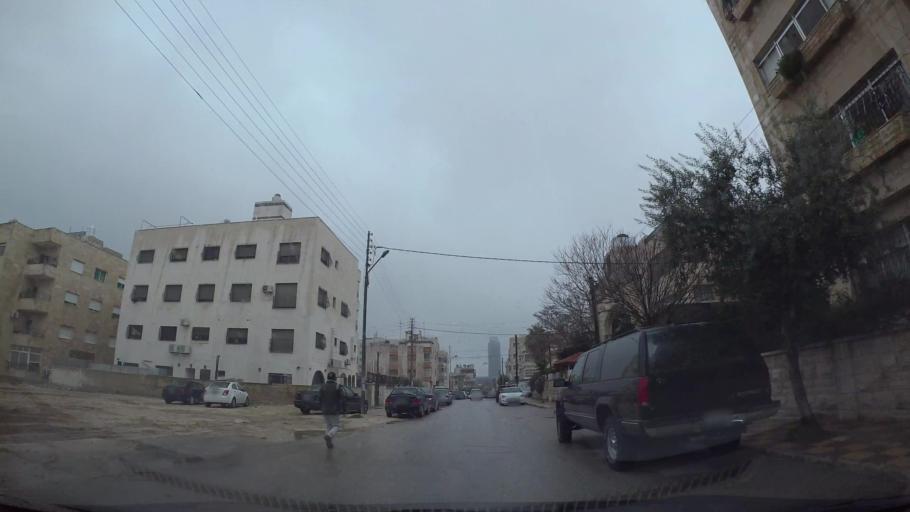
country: JO
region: Amman
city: Amman
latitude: 31.9705
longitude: 35.9169
